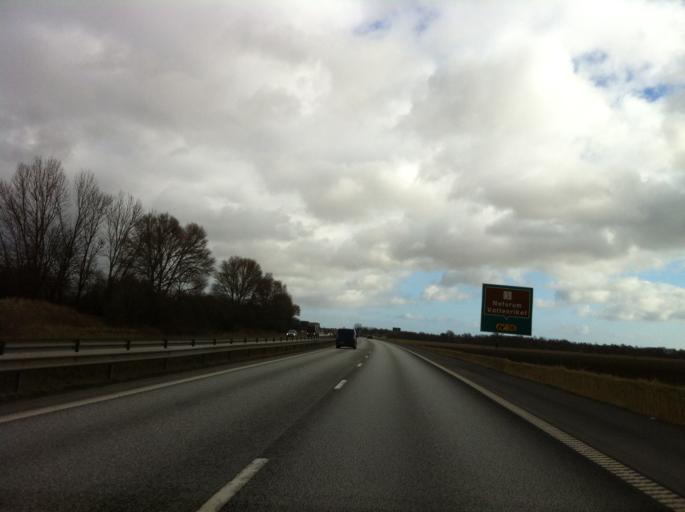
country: SE
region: Skane
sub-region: Kristianstads Kommun
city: Kristianstad
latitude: 56.0204
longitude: 14.1089
